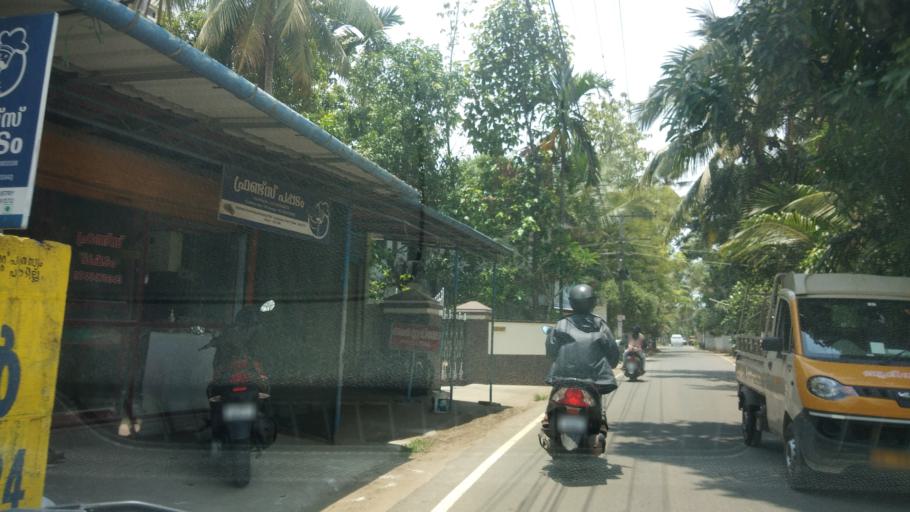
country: IN
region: Kerala
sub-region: Alappuzha
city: Arukutti
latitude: 9.8955
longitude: 76.3092
